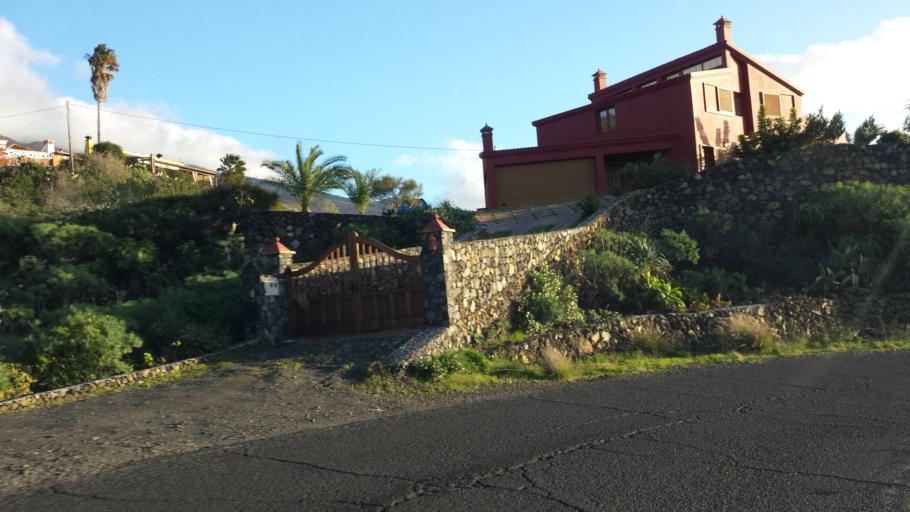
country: ES
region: Canary Islands
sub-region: Provincia de Santa Cruz de Tenerife
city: El Paso
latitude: 28.6199
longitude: -17.8843
